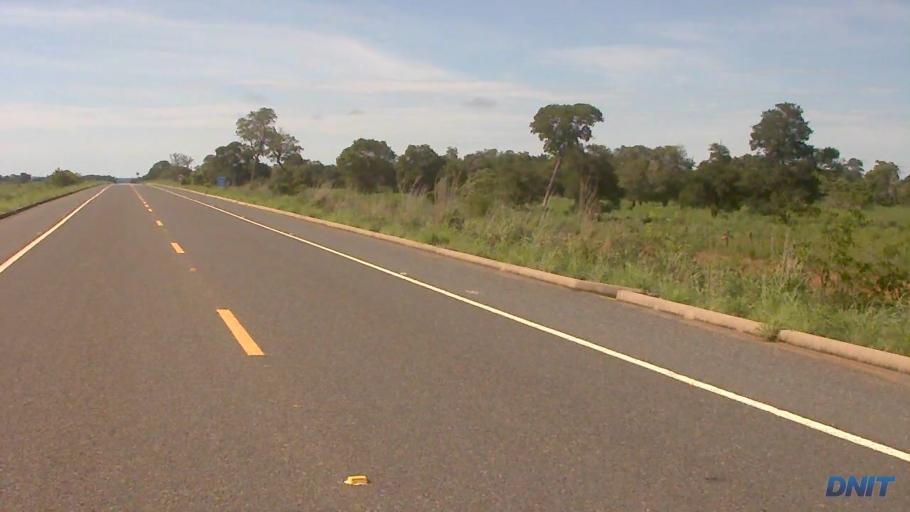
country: BR
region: Goias
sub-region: Sao Miguel Do Araguaia
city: Sao Miguel do Araguaia
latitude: -13.4324
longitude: -50.1259
